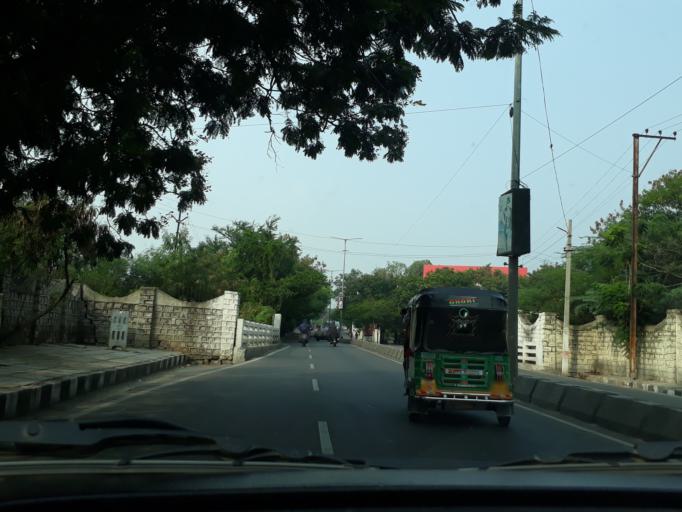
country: IN
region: Telangana
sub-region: Hyderabad
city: Malkajgiri
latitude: 17.4459
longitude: 78.4915
